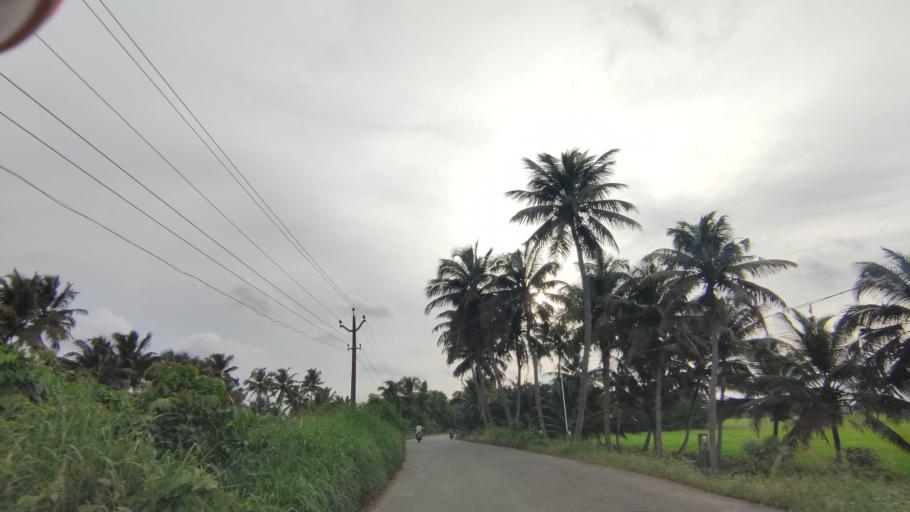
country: IN
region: Kerala
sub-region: Kottayam
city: Vaikam
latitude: 9.6830
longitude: 76.4483
